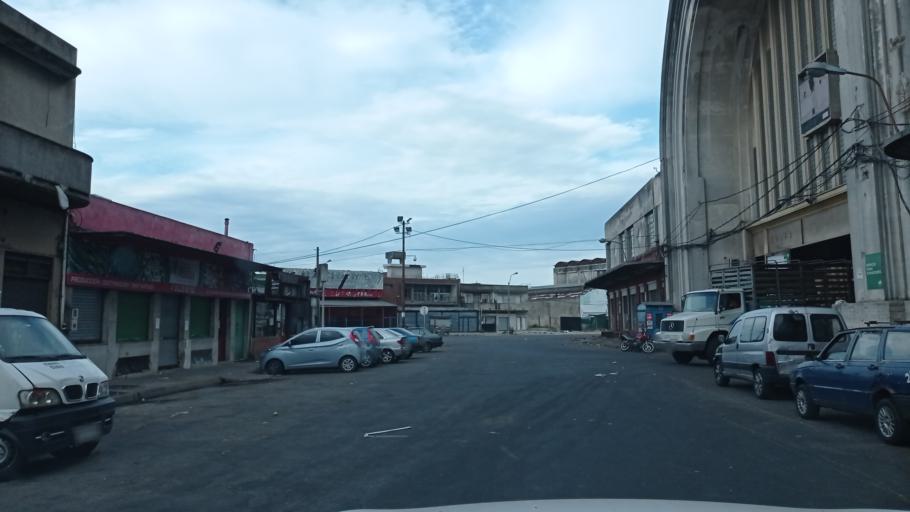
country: UY
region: Montevideo
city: Montevideo
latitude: -34.8718
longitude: -56.1550
